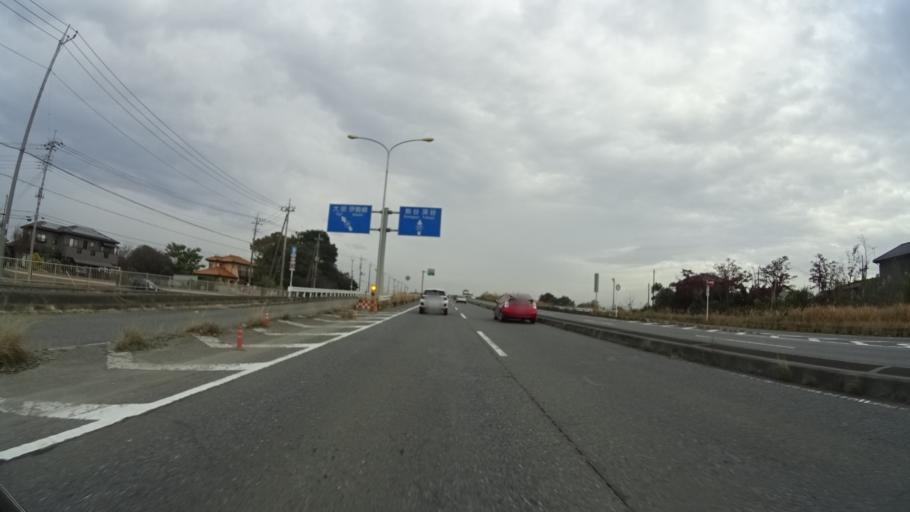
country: JP
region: Gunma
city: Isesaki
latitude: 36.3647
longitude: 139.1704
